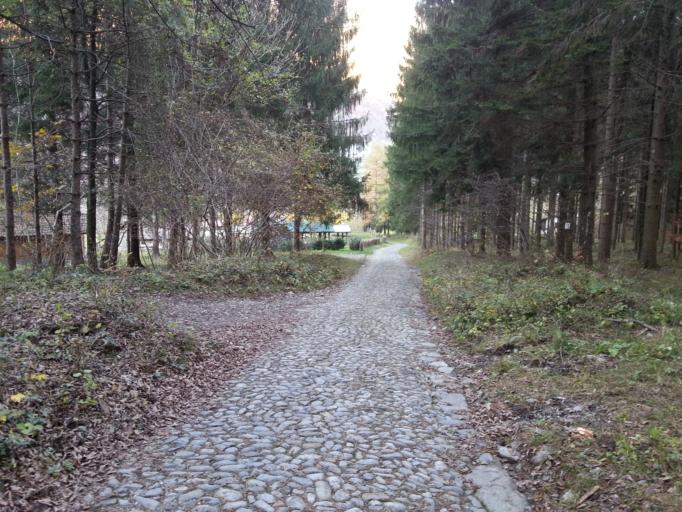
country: IT
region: Lombardy
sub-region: Provincia di Lecco
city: Primaluna
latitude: 45.9803
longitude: 9.4193
